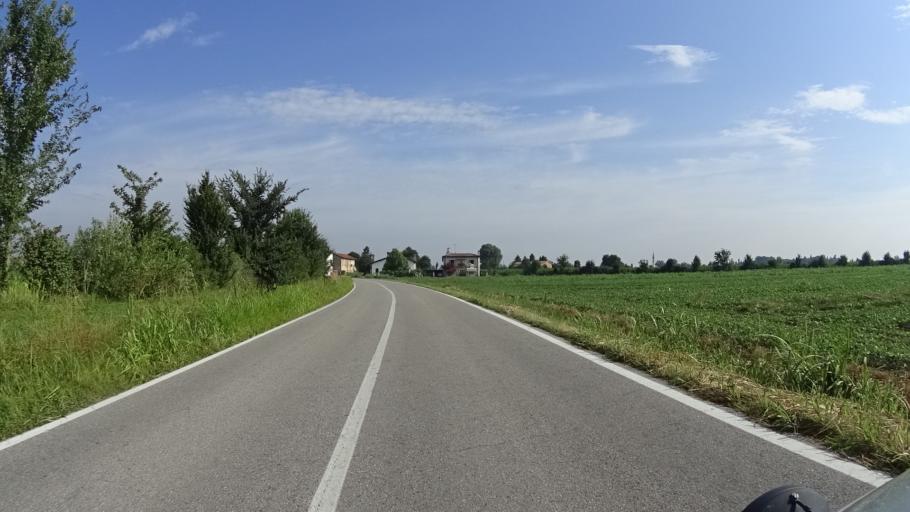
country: IT
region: Veneto
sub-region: Provincia di Venezia
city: Lugugnana
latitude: 45.7176
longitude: 12.9495
